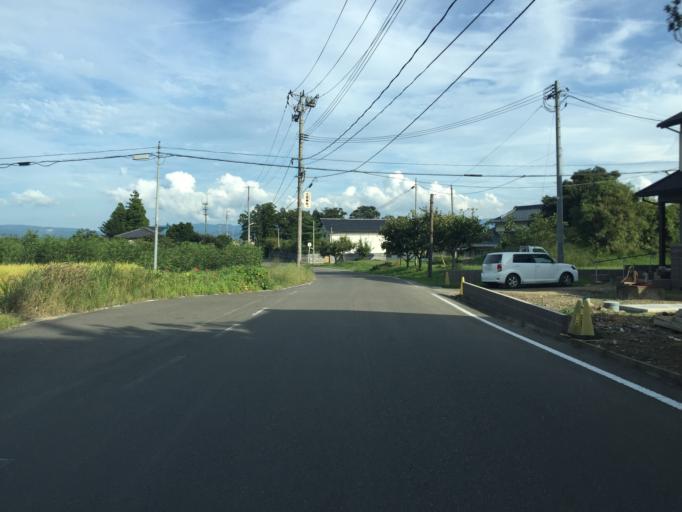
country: JP
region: Fukushima
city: Hobaramachi
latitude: 37.8820
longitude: 140.5382
